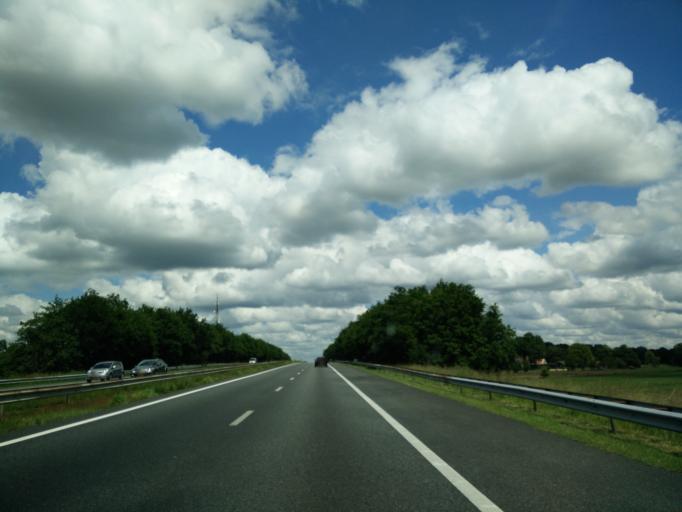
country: NL
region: Drenthe
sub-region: Gemeente Tynaarlo
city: Vries
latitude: 53.0442
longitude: 6.5882
